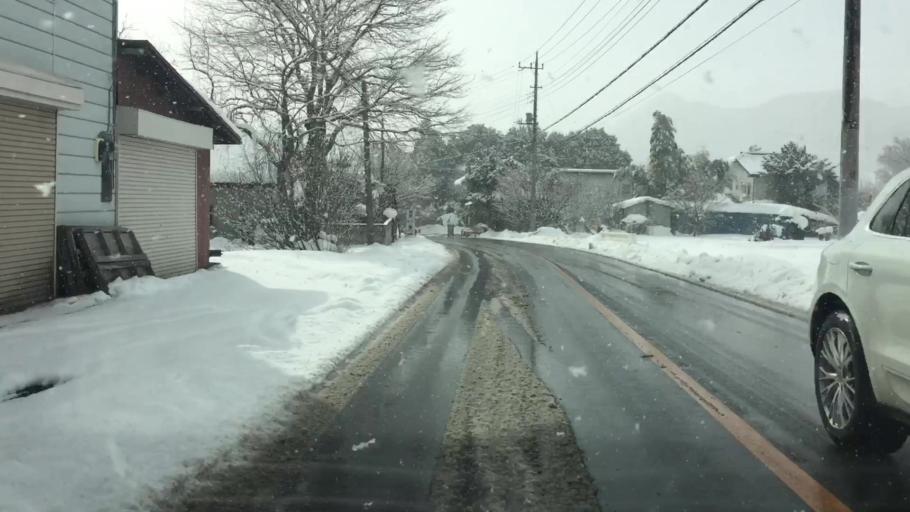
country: JP
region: Gunma
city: Numata
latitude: 36.7011
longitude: 139.0651
